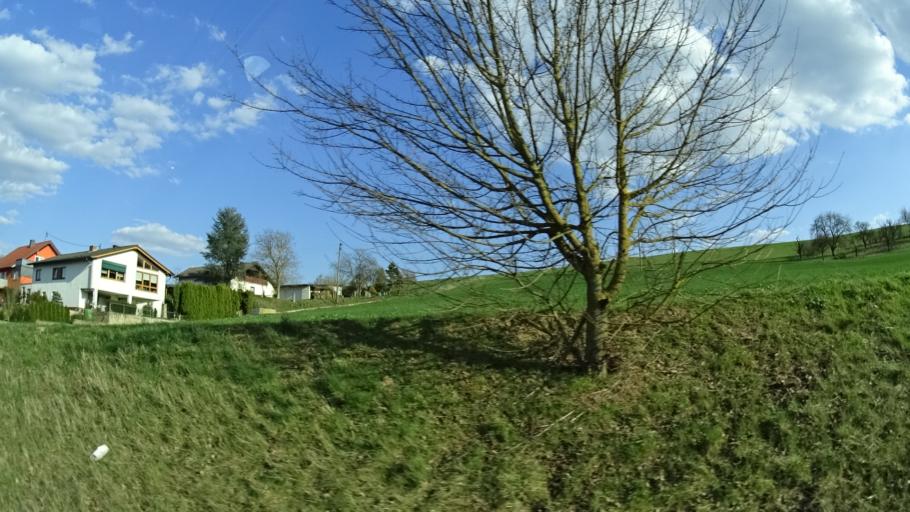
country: DE
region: Rheinland-Pfalz
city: Rehborn
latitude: 49.7328
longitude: 7.6802
